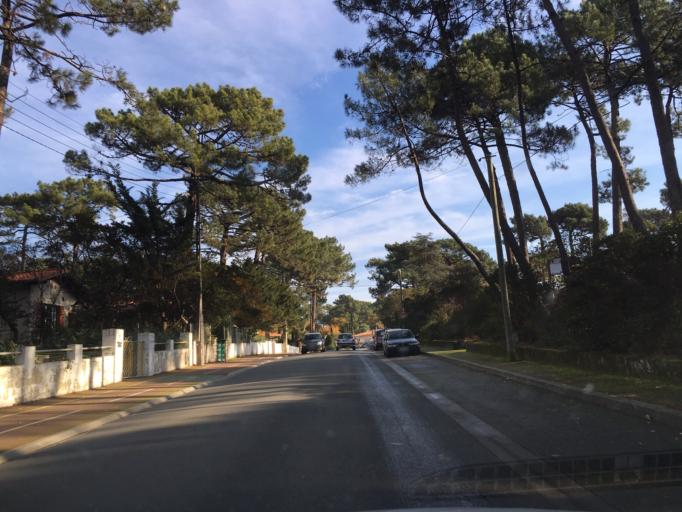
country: FR
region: Aquitaine
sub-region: Departement de la Gironde
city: Arcachon
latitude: 44.6477
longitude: -1.1829
